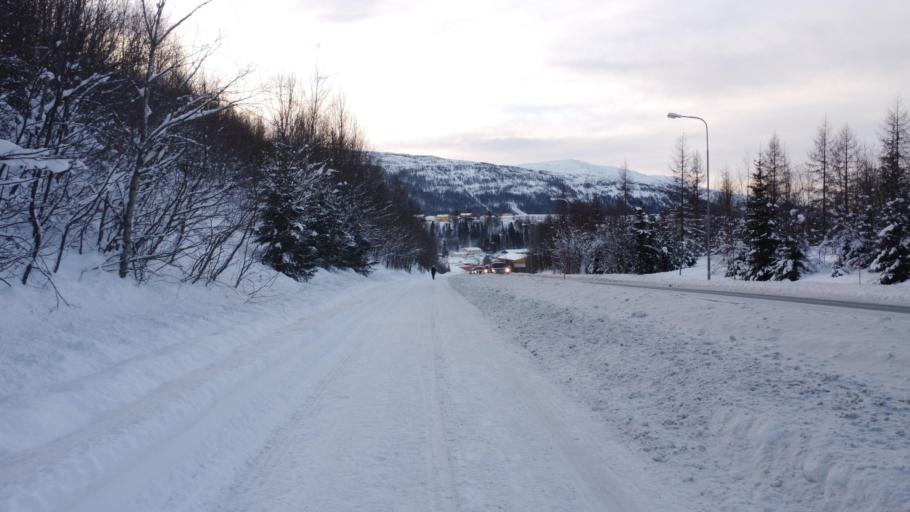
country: NO
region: Nordland
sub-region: Rana
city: Mo i Rana
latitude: 66.3222
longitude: 14.1573
